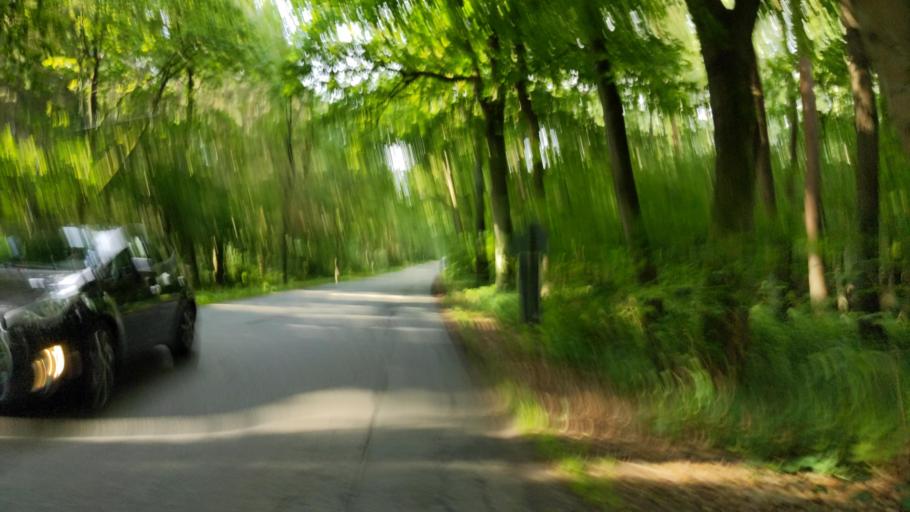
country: DE
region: Schleswig-Holstein
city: Ratekau
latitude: 53.9772
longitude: 10.7031
